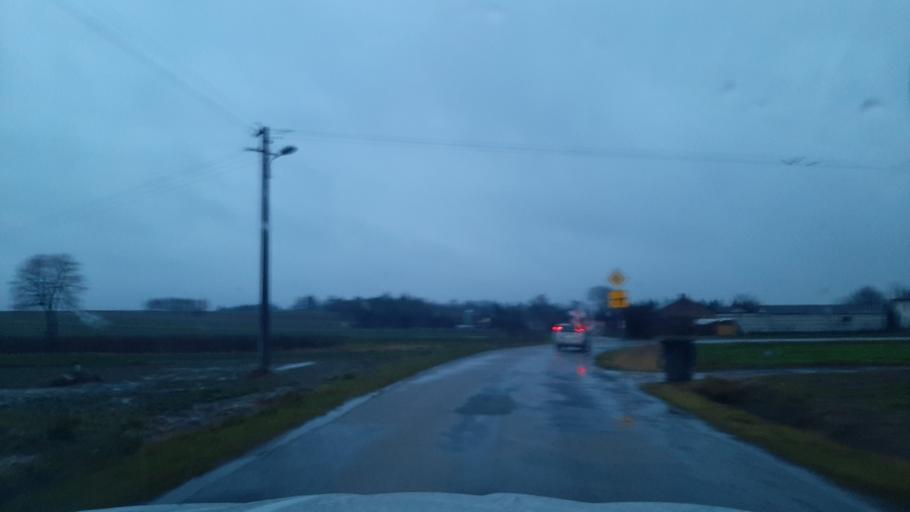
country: PL
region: Lublin Voivodeship
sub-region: Powiat lubelski
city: Jastkow
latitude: 51.3639
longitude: 22.4534
